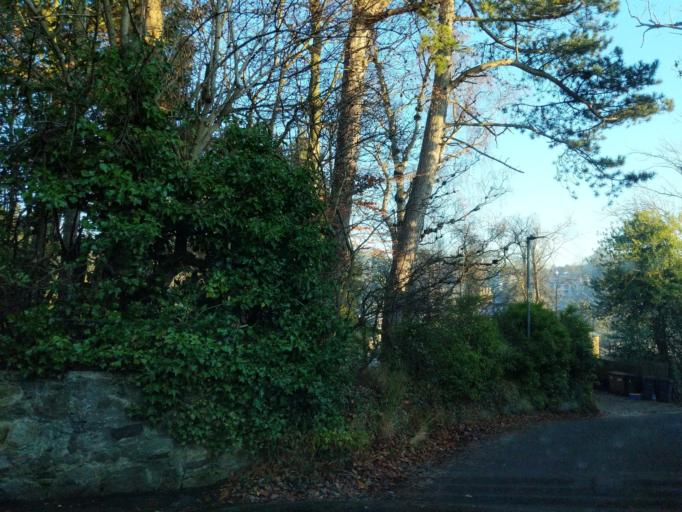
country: GB
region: Scotland
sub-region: Edinburgh
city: Colinton
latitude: 55.9091
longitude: -3.2585
